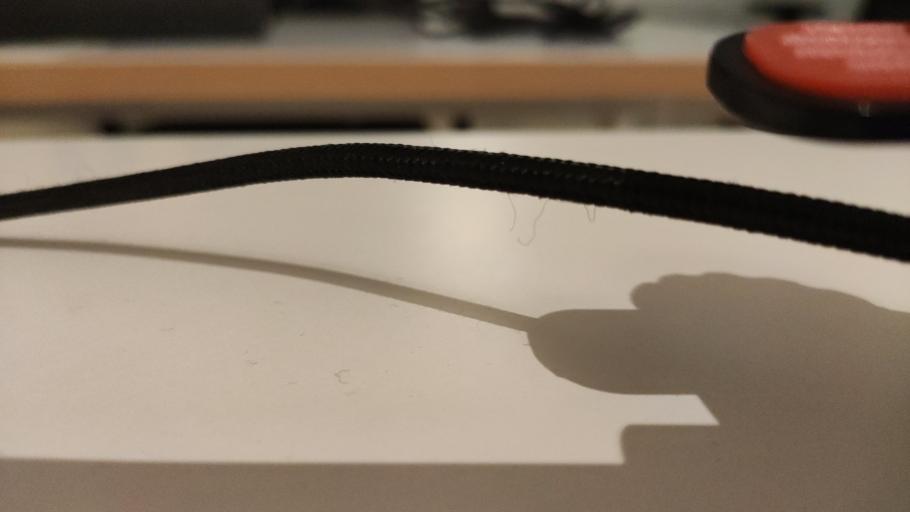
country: RU
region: Moskovskaya
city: Il'inskiy Pogost
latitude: 55.5289
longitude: 38.8723
